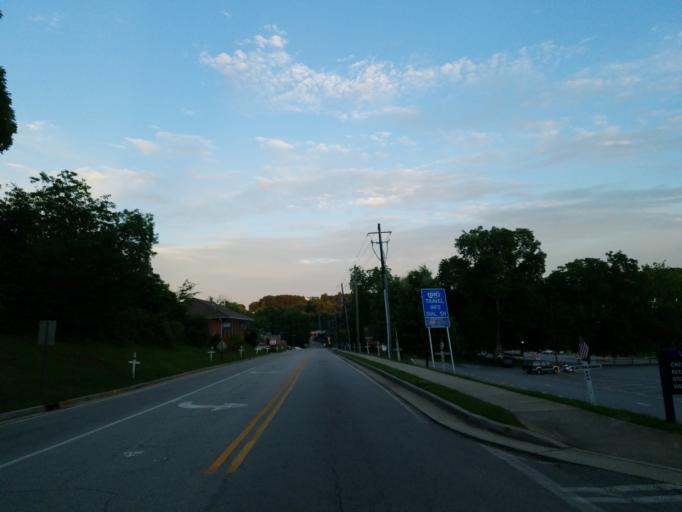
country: US
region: Georgia
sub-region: Lumpkin County
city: Dahlonega
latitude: 34.5304
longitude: -83.9831
